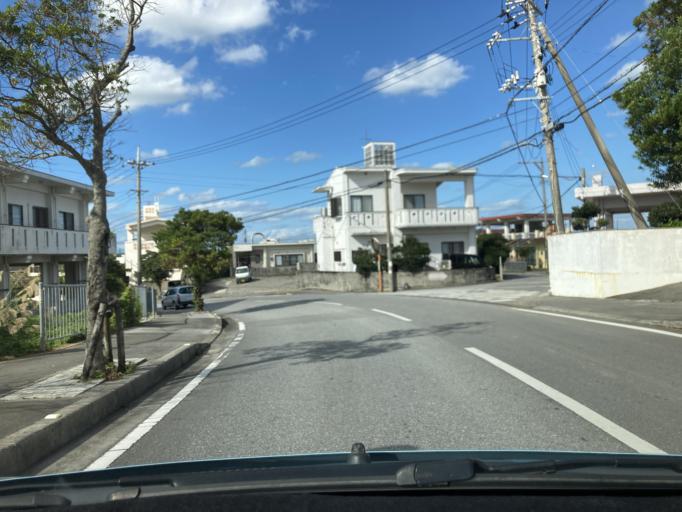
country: JP
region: Okinawa
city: Gushikawa
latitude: 26.3672
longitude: 127.8435
